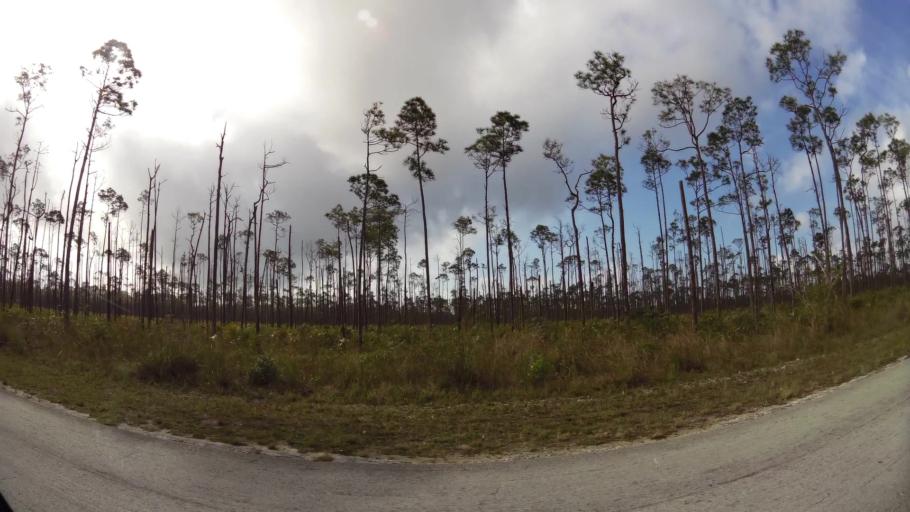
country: BS
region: Freeport
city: Lucaya
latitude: 26.5924
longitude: -78.5539
